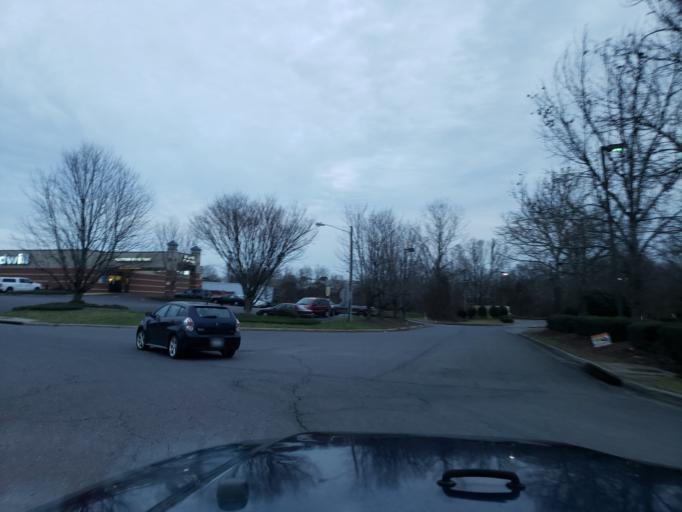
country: US
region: North Carolina
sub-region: Cleveland County
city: Shelby
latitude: 35.2777
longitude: -81.5336
